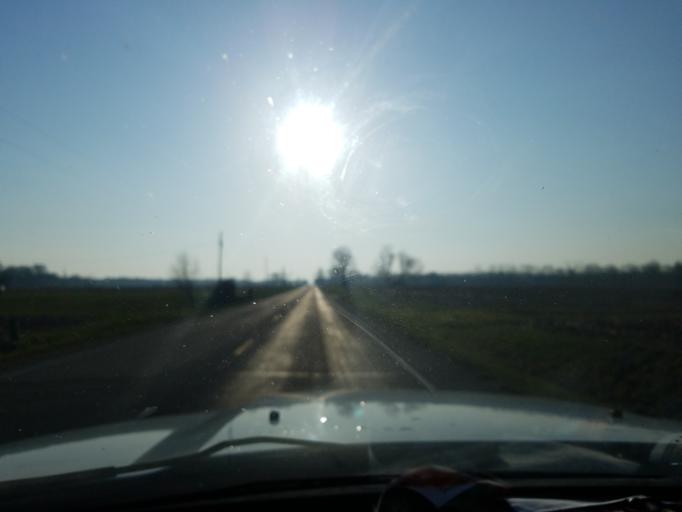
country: US
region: Indiana
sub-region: Vigo County
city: Seelyville
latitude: 39.3886
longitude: -87.1861
